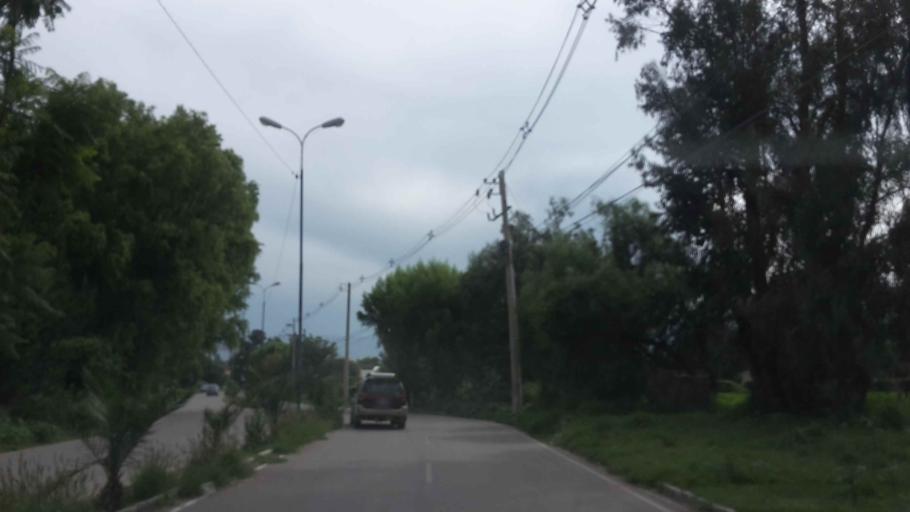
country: BO
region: Cochabamba
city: Cochabamba
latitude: -17.3291
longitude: -66.2474
